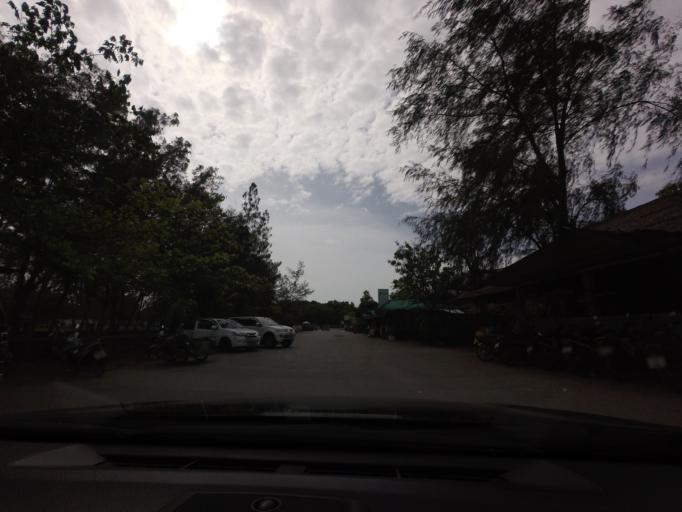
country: TH
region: Pattani
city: Pattani
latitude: 6.8949
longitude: 101.2459
